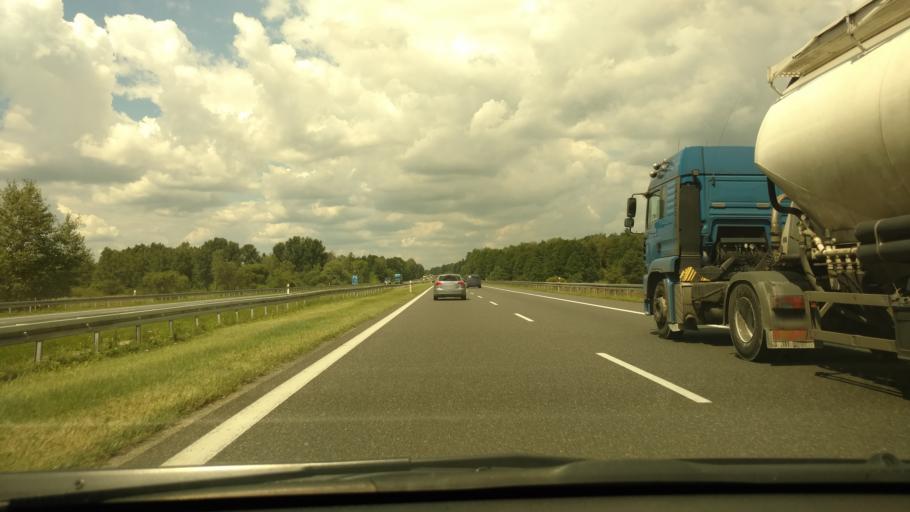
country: PL
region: Lesser Poland Voivodeship
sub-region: Powiat chrzanowski
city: Bolecin
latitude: 50.1237
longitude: 19.4901
